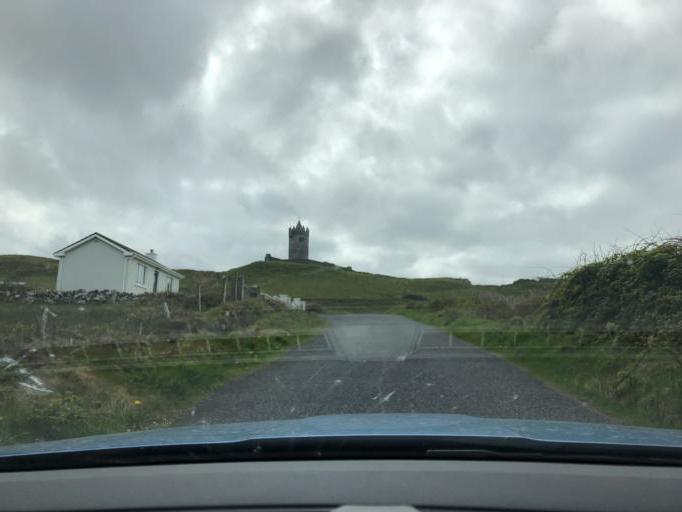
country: IE
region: Connaught
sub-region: County Galway
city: Bearna
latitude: 53.0061
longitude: -9.3882
